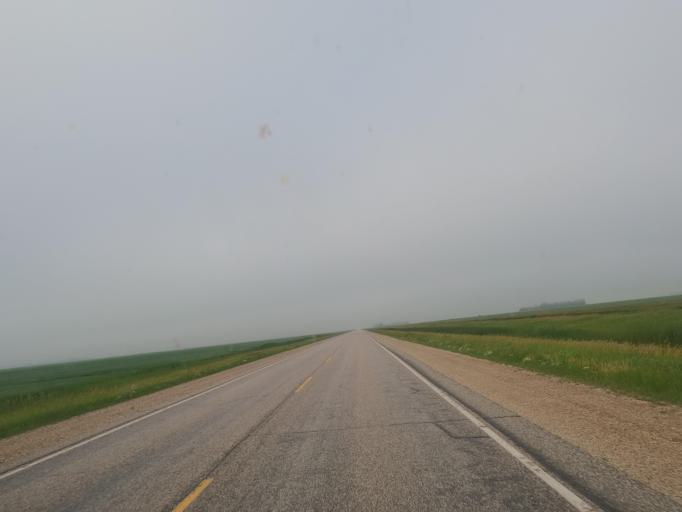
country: CA
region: Manitoba
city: Carman
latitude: 49.7339
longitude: -97.8493
